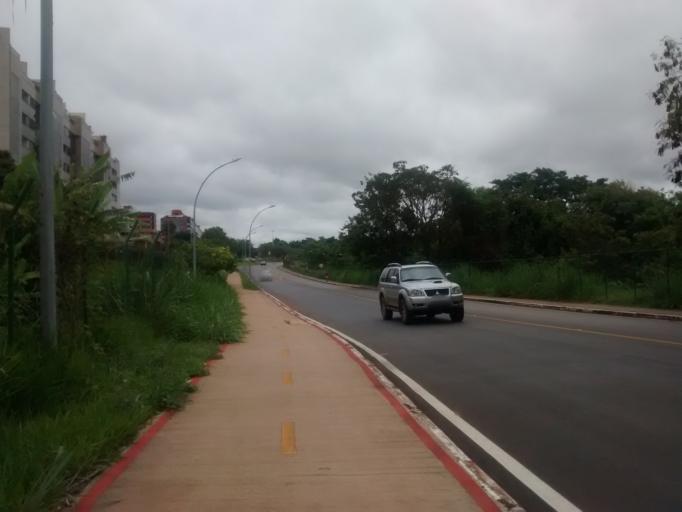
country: BR
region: Federal District
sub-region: Brasilia
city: Brasilia
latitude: -15.7473
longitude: -47.8853
